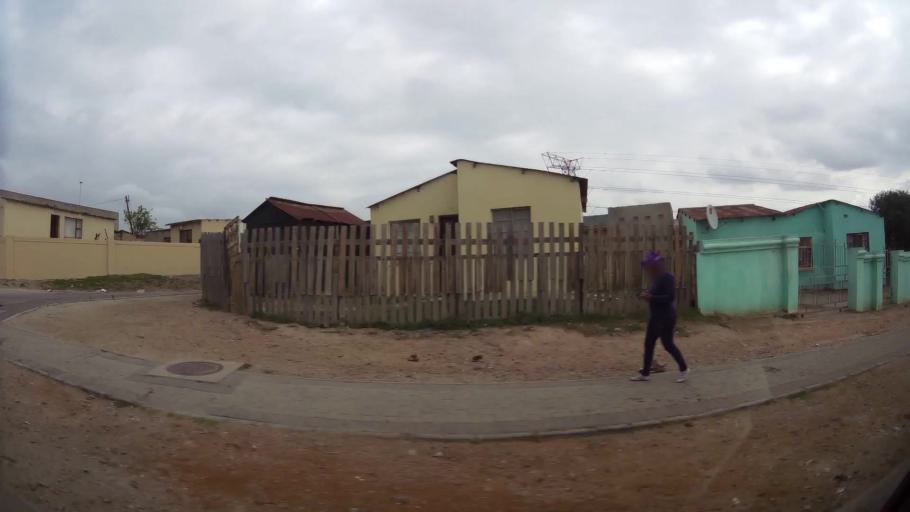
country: ZA
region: Eastern Cape
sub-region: Nelson Mandela Bay Metropolitan Municipality
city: Port Elizabeth
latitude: -33.8903
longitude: 25.5951
